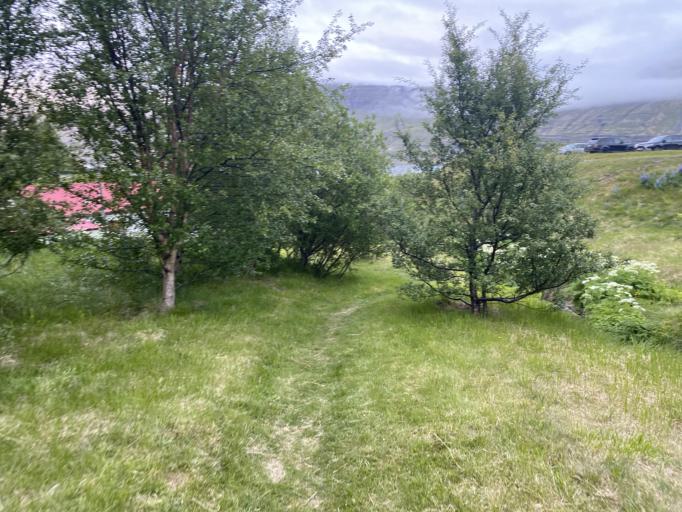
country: IS
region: East
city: Reydarfjoerdur
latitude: 65.0341
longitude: -14.2061
